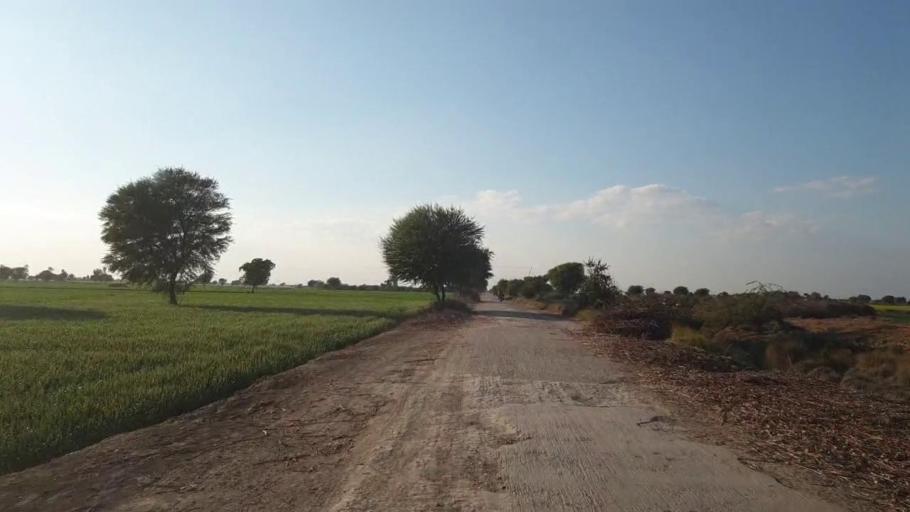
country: PK
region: Sindh
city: Shahpur Chakar
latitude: 26.1387
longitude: 68.5539
